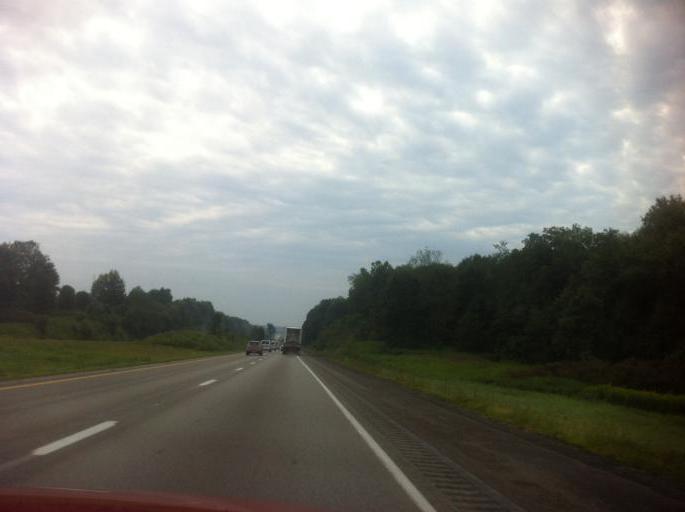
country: US
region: Pennsylvania
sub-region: Mercer County
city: Grove City
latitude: 41.2009
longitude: -80.0438
